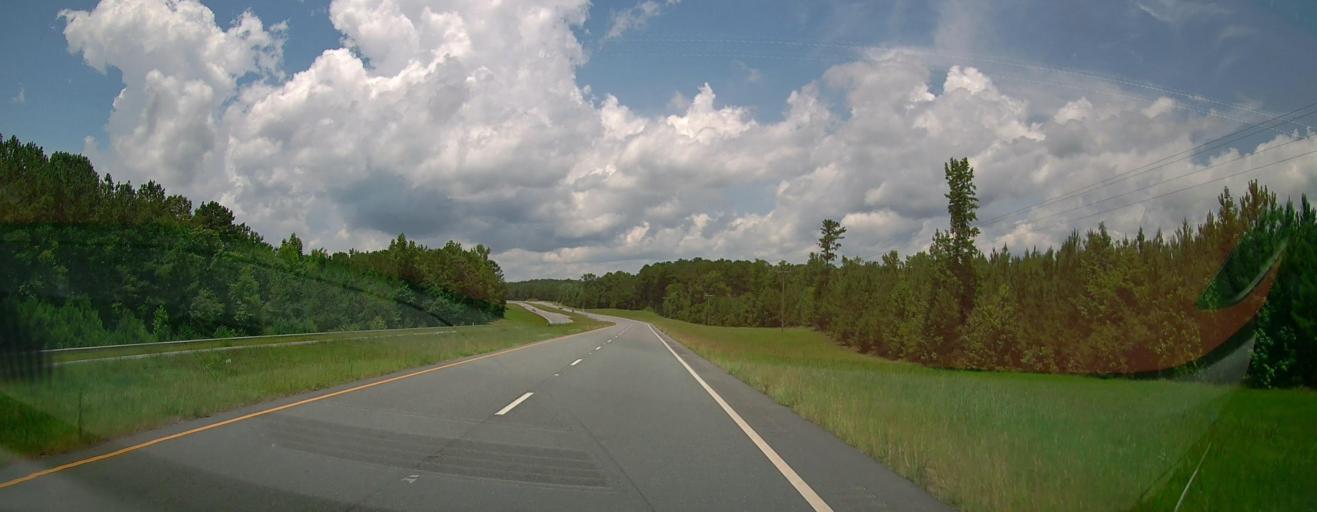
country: US
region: Georgia
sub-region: Upson County
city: Thomaston
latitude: 32.7811
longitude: -84.2456
